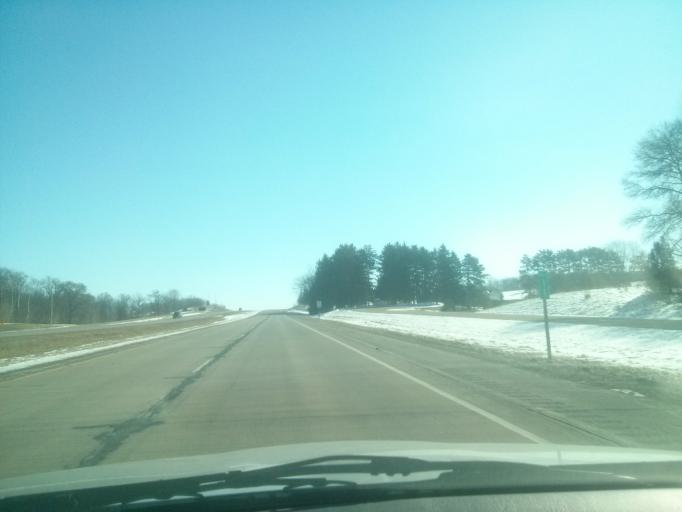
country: US
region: Wisconsin
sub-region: Saint Croix County
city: Somerset
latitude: 45.1228
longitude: -92.6270
